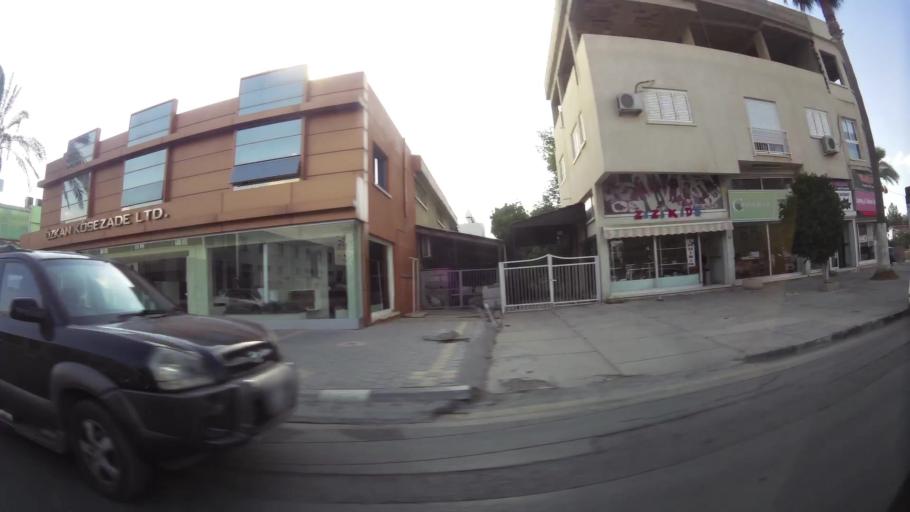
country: CY
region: Lefkosia
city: Nicosia
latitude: 35.1993
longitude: 33.3675
